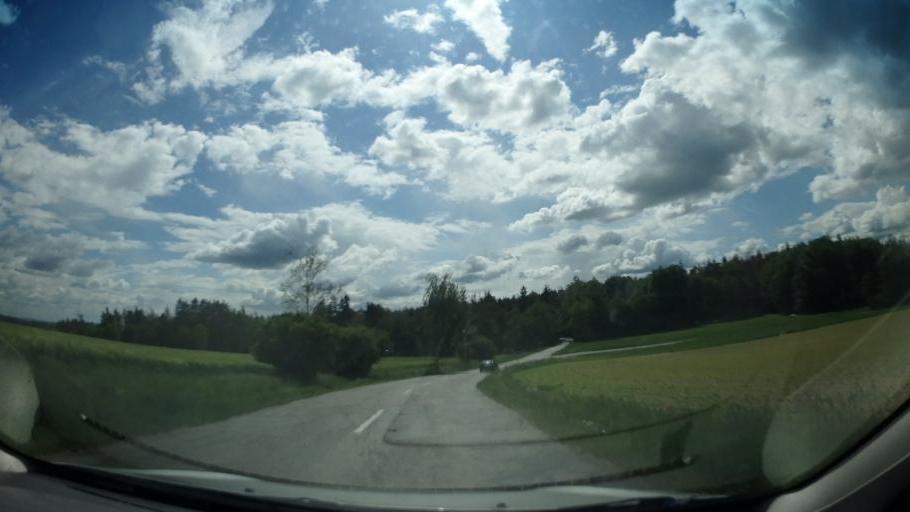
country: CZ
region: South Moravian
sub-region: Okres Blansko
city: Letovice
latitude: 49.5833
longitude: 16.5909
